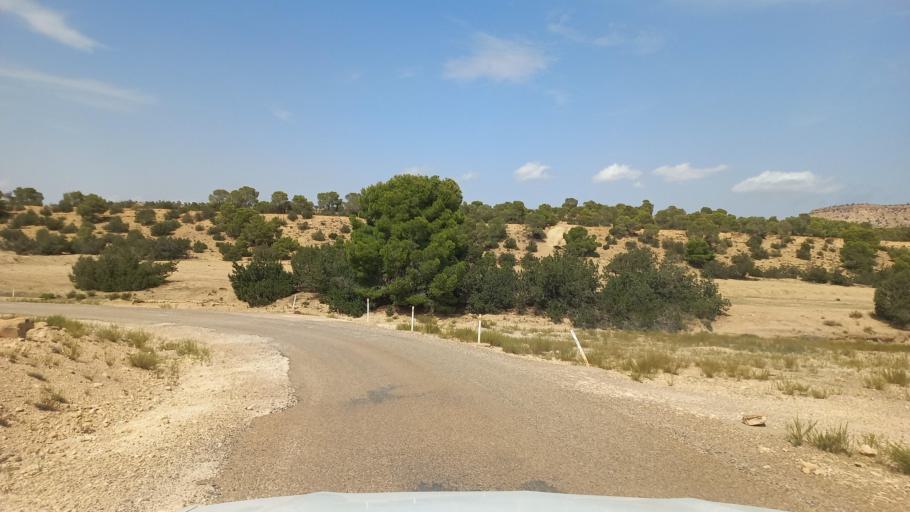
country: TN
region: Al Qasrayn
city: Sbiba
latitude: 35.4098
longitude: 8.9298
